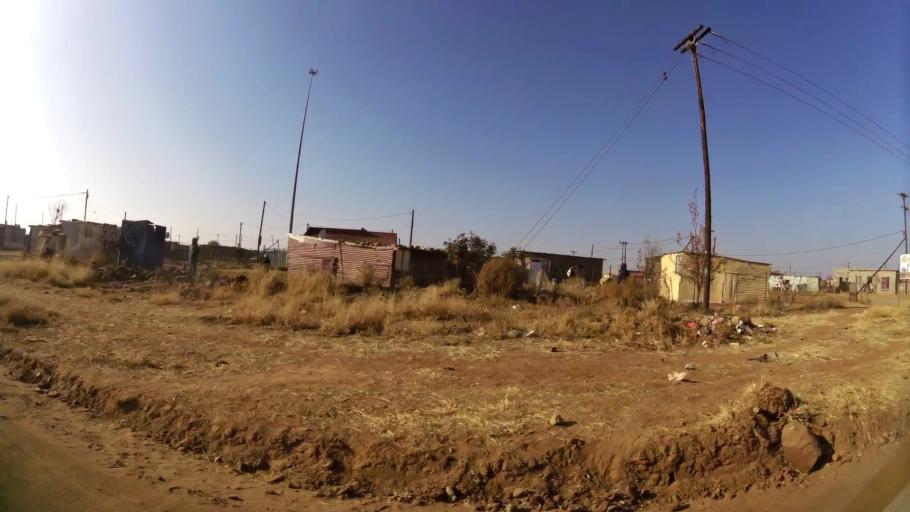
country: ZA
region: Orange Free State
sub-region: Mangaung Metropolitan Municipality
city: Bloemfontein
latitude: -29.2028
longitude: 26.2530
